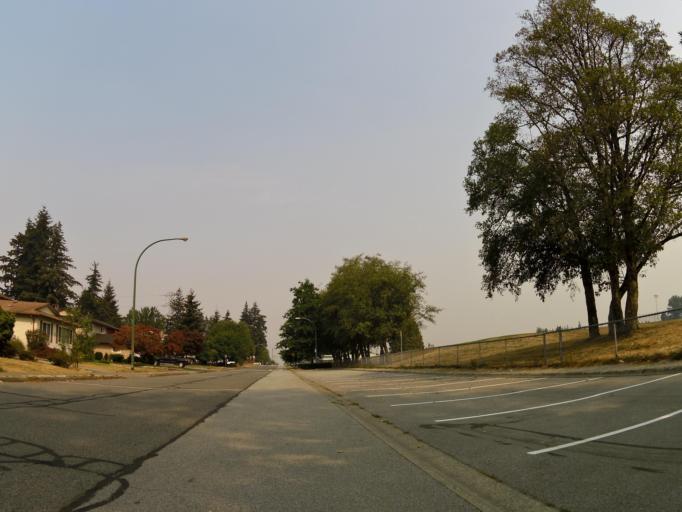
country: CA
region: British Columbia
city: Delta
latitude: 49.1492
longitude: -122.9240
